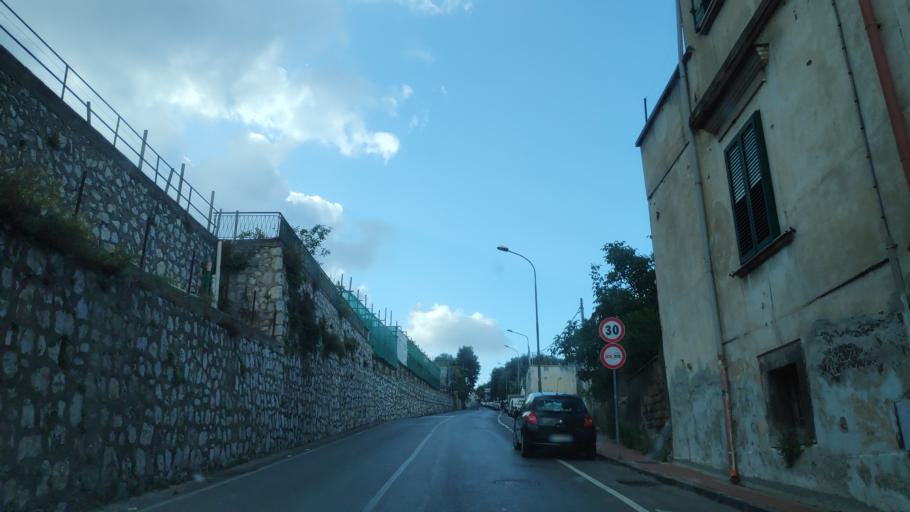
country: IT
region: Campania
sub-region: Provincia di Napoli
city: Piano di Sorrento
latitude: 40.6313
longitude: 14.4198
